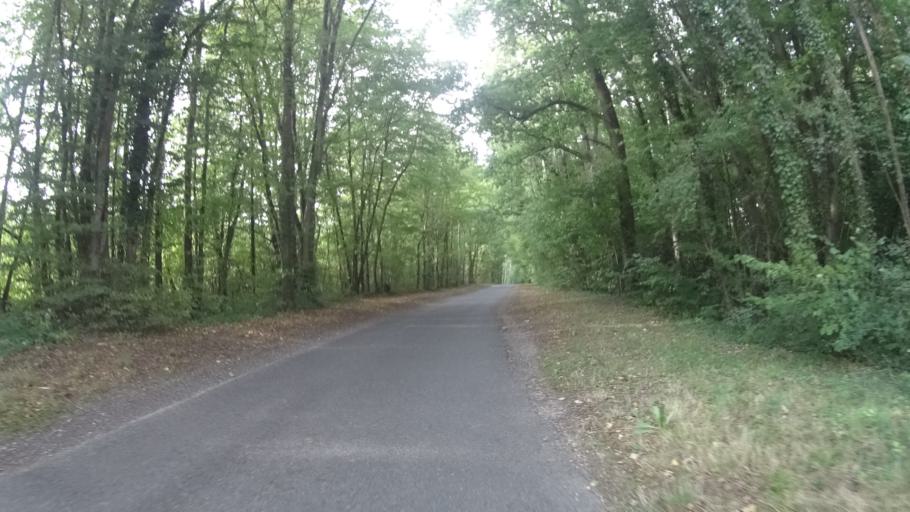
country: FR
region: Picardie
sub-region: Departement de l'Oise
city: Ver-sur-Launette
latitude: 49.1679
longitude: 2.6801
